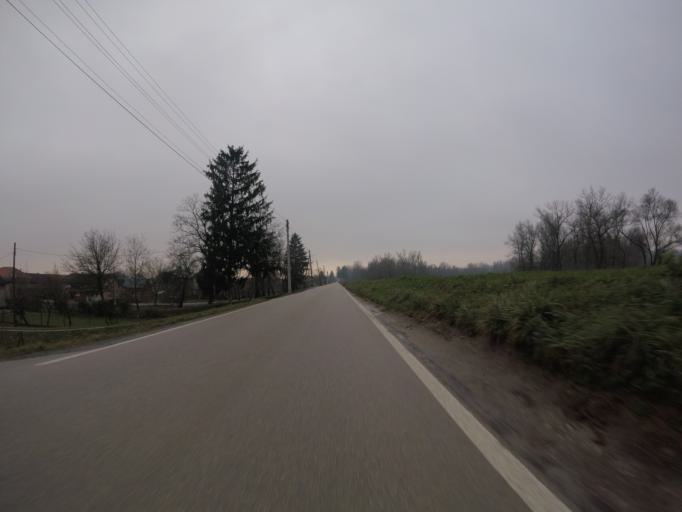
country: HR
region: Zagrebacka
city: Kuce
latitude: 45.6939
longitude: 16.2253
